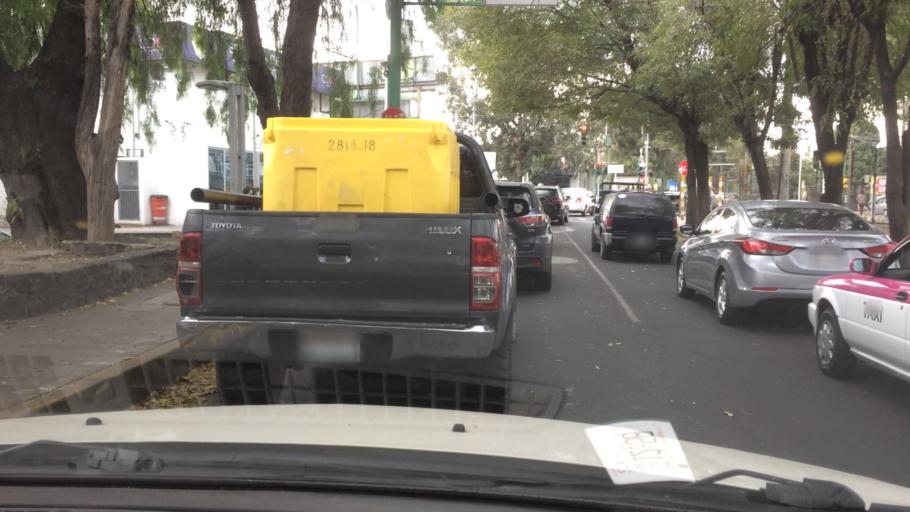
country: MX
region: Mexico City
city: Tlalpan
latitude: 19.2809
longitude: -99.1371
